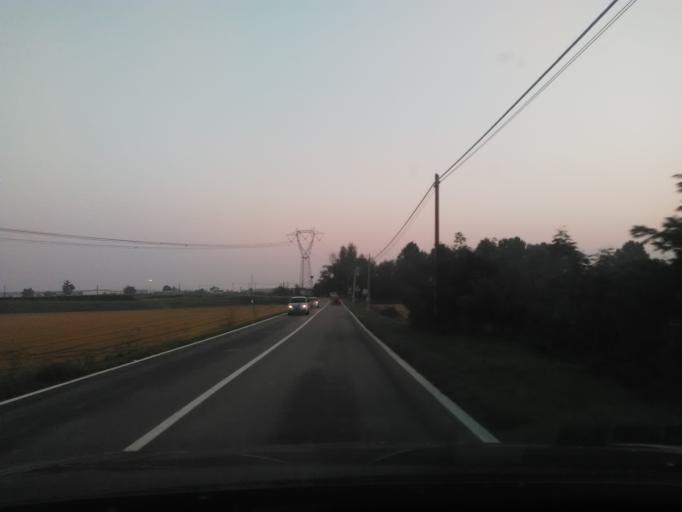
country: IT
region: Piedmont
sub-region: Provincia di Vercelli
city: Carisio
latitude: 45.4207
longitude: 8.2095
